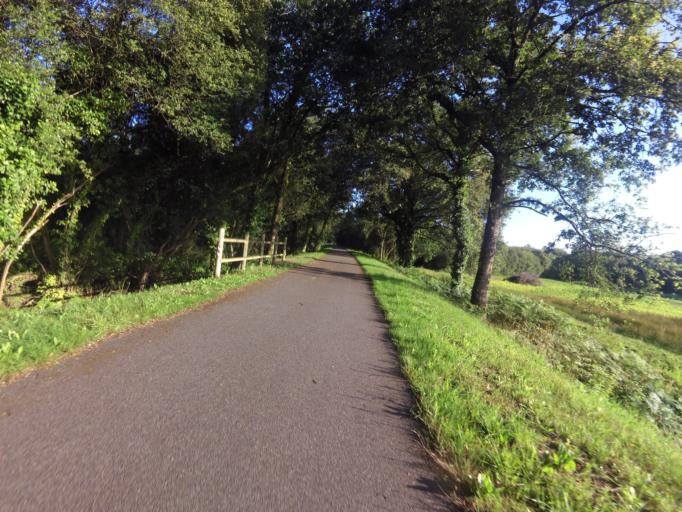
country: FR
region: Brittany
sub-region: Departement du Morbihan
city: Malestroit
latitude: 47.8331
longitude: -2.4212
